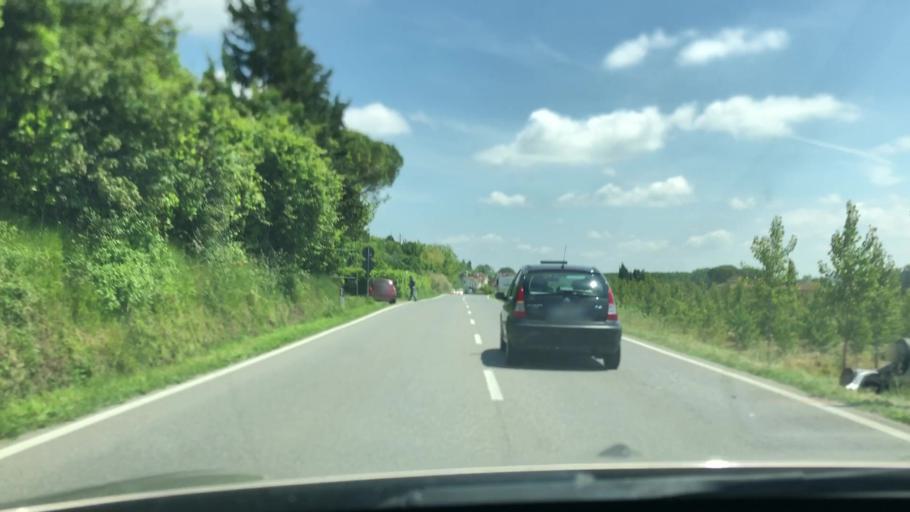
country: IT
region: Tuscany
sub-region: Province of Pisa
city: Treggiaia
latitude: 43.6121
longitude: 10.6851
